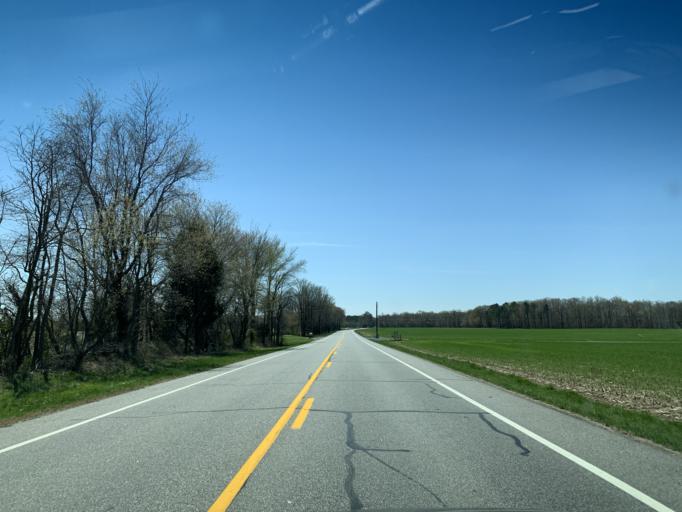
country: US
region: Maryland
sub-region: Talbot County
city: Easton
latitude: 38.8284
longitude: -76.0354
